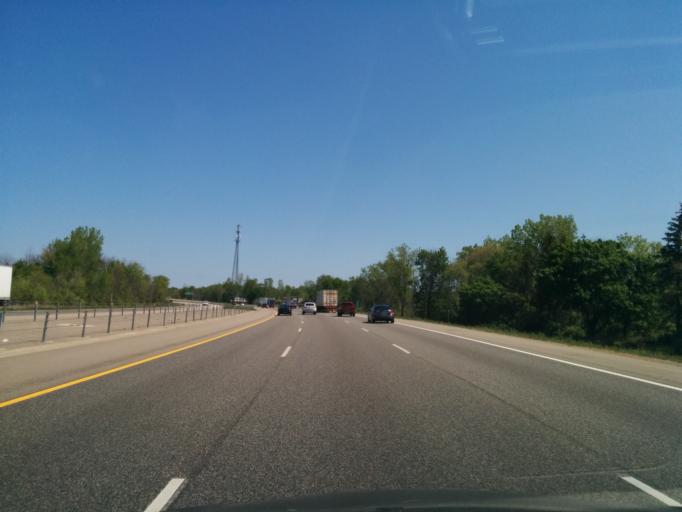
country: US
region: Michigan
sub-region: Berrien County
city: Bridgman
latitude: 41.9211
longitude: -86.5709
